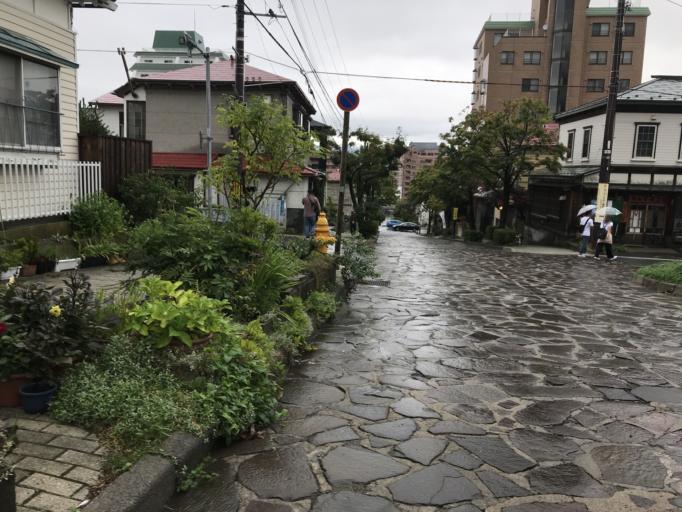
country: JP
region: Hokkaido
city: Hakodate
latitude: 41.7636
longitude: 140.7138
